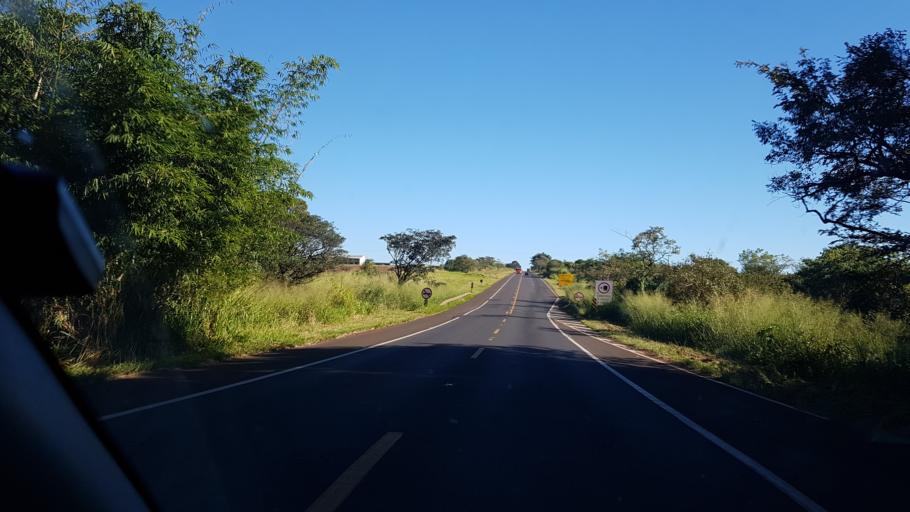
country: BR
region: Sao Paulo
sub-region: Assis
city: Assis
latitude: -22.6032
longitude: -50.4766
